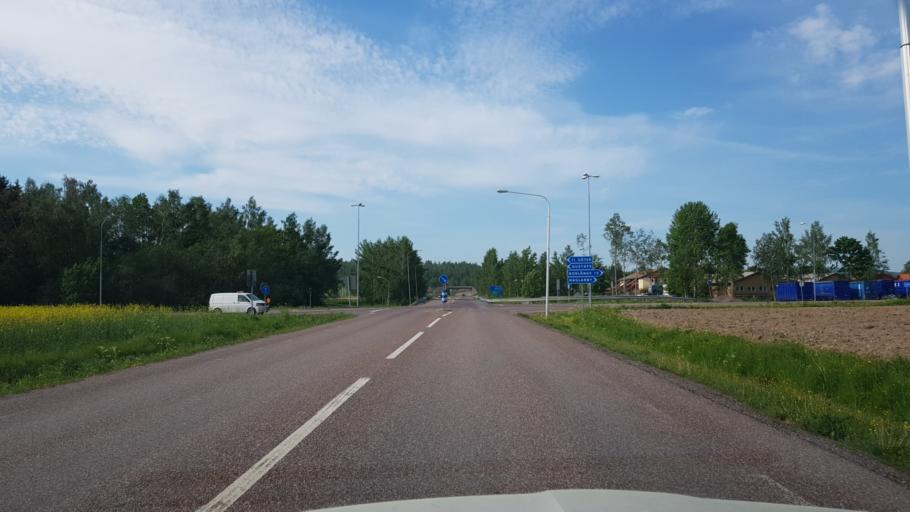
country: SE
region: Dalarna
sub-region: Borlange Kommun
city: Ornas
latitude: 60.4154
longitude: 15.5955
